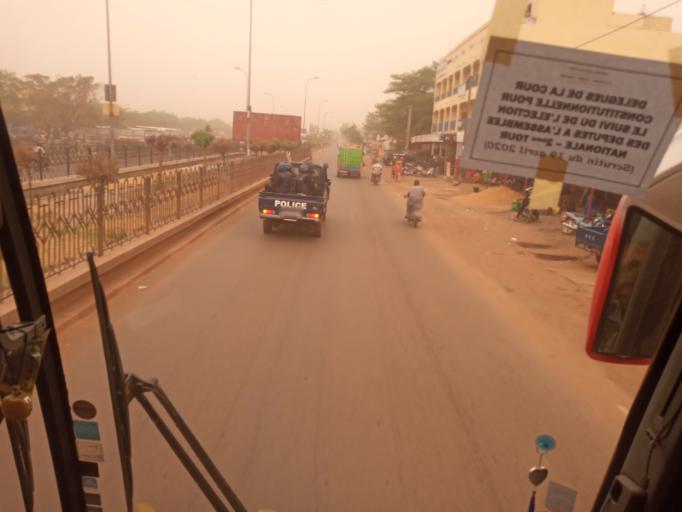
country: ML
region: Bamako
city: Bamako
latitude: 12.6528
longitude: -7.9839
